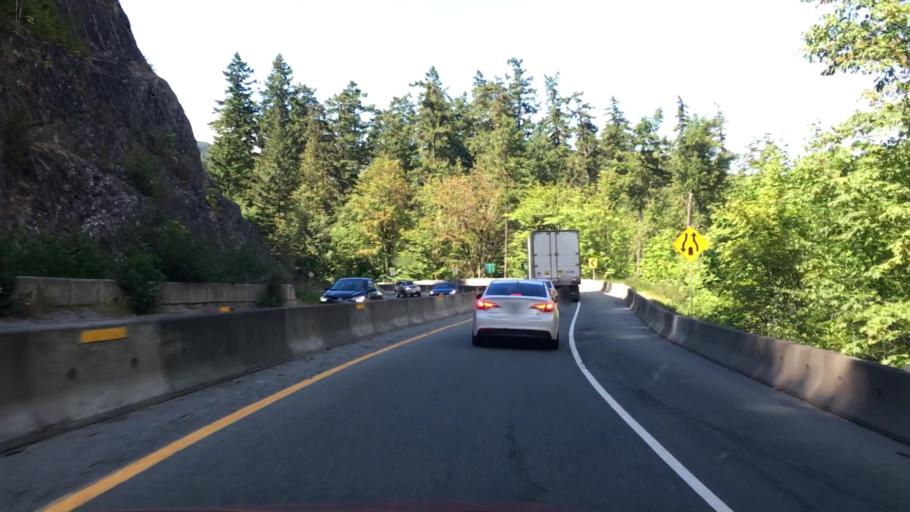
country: CA
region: British Columbia
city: Port Alberni
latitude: 49.2524
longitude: -124.6622
